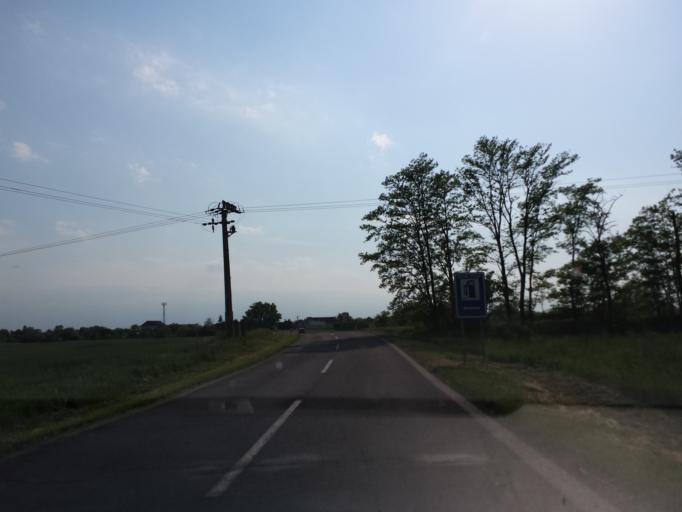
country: AT
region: Lower Austria
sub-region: Politischer Bezirk Ganserndorf
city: Angern an der March
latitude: 48.3888
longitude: 16.8652
